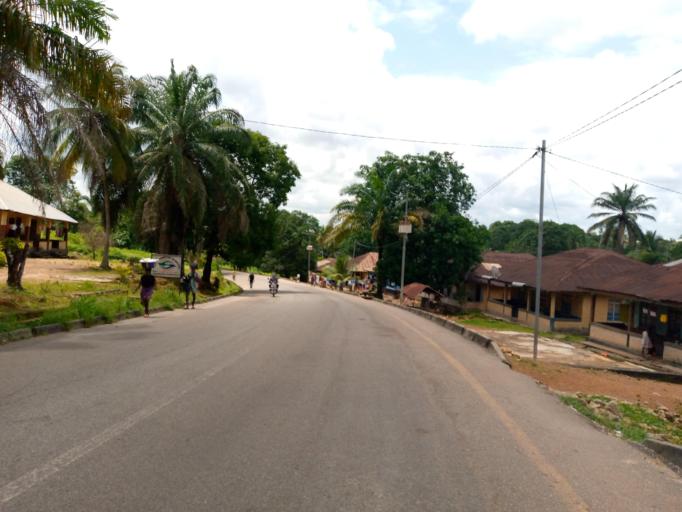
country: SL
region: Northern Province
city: Magburaka
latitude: 8.7268
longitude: -11.9467
